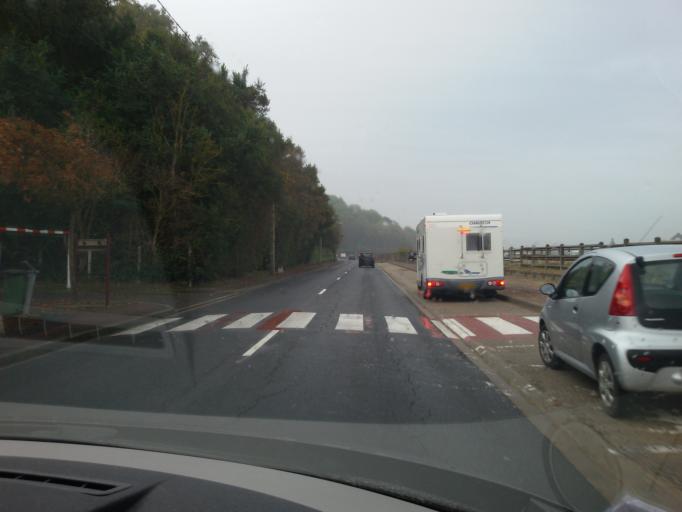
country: FR
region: Lower Normandy
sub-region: Departement du Calvados
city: Houlgate
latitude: 49.2983
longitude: -0.0856
